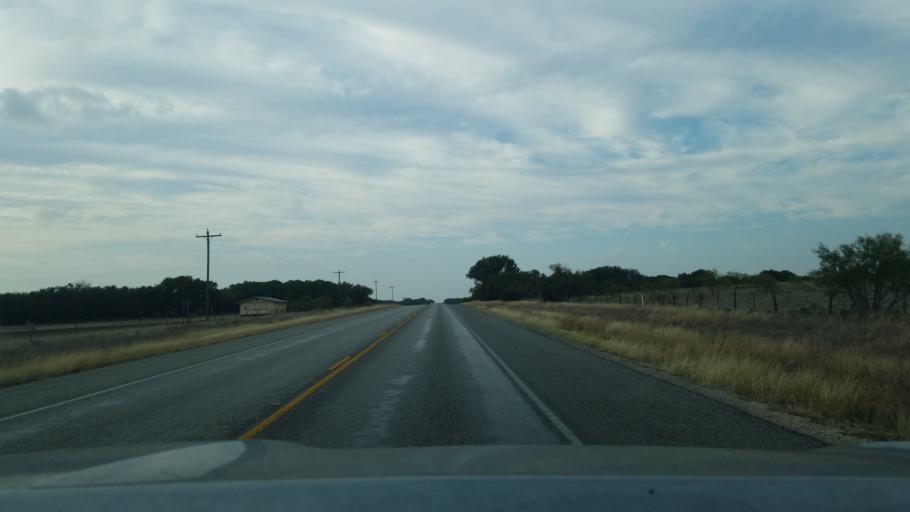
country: US
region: Texas
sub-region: Mills County
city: Goldthwaite
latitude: 31.5302
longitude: -98.6101
